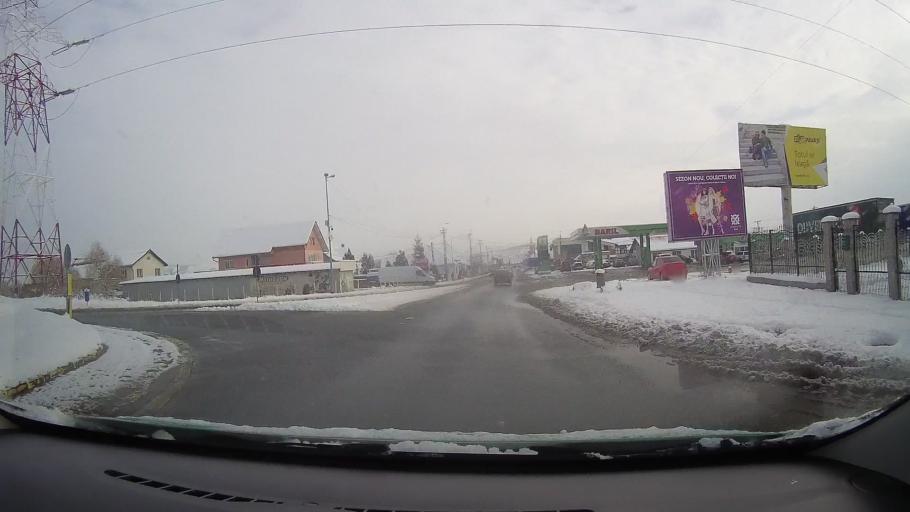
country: RO
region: Alba
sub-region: Municipiul Sebes
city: Sebes
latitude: 45.9595
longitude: 23.5522
